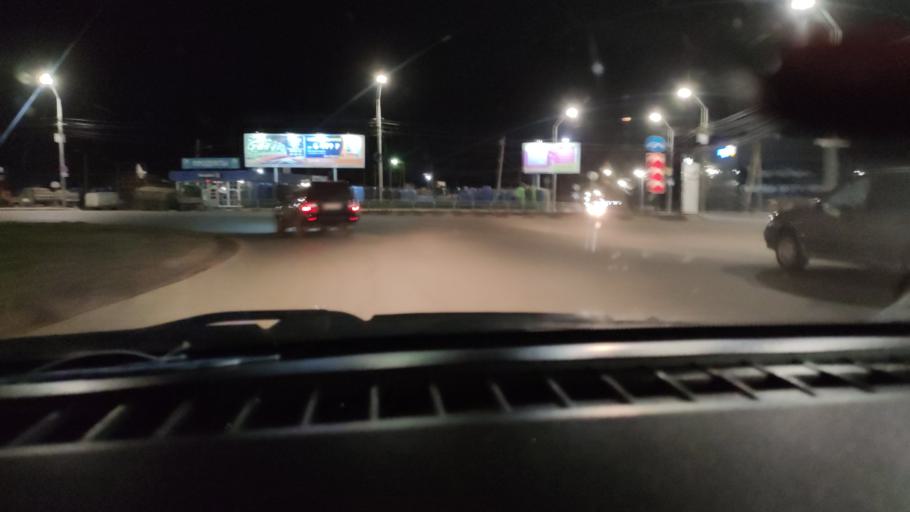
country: RU
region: Saratov
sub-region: Saratovskiy Rayon
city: Saratov
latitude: 51.5582
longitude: 46.0677
